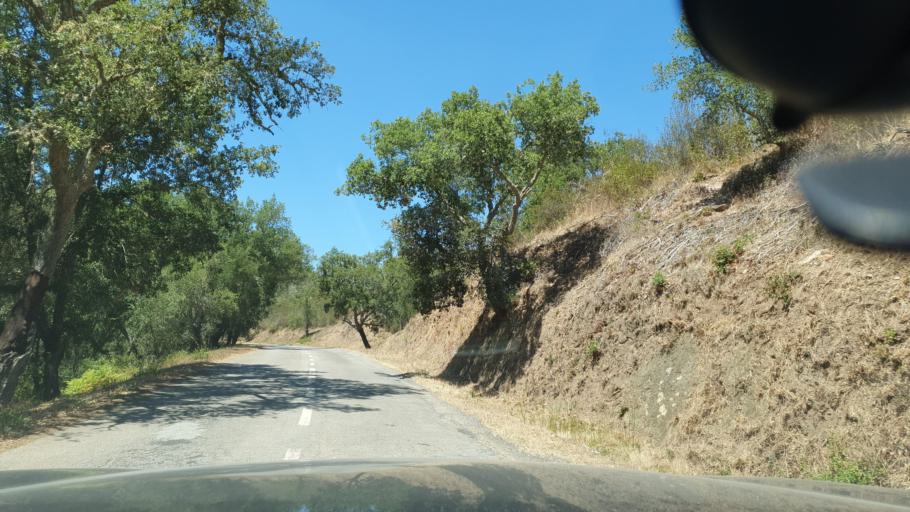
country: PT
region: Beja
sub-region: Odemira
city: Odemira
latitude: 37.5988
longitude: -8.4933
